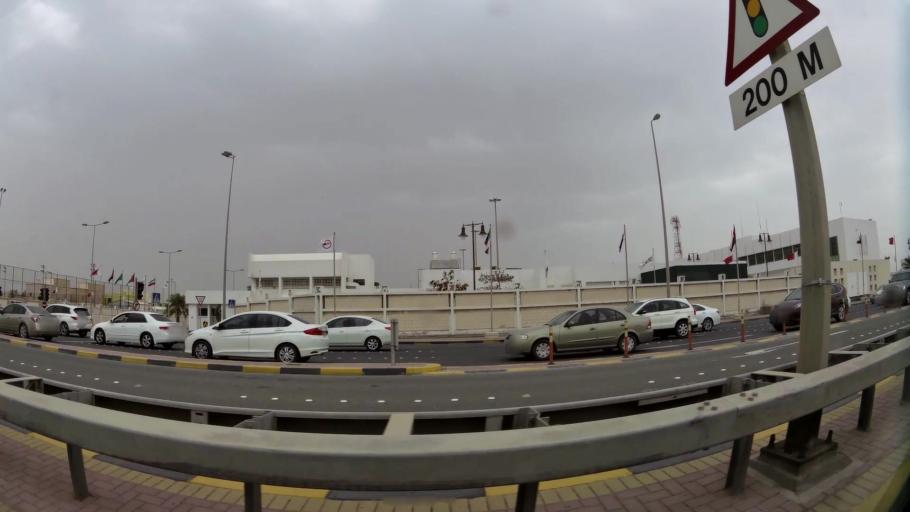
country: BH
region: Northern
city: Madinat `Isa
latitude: 26.1553
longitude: 50.5416
